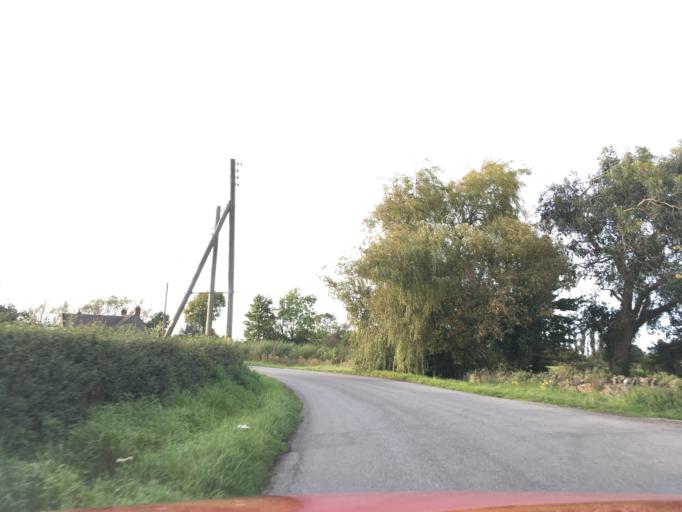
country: GB
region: England
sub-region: South Gloucestershire
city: Severn Beach
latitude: 51.5752
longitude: -2.6341
